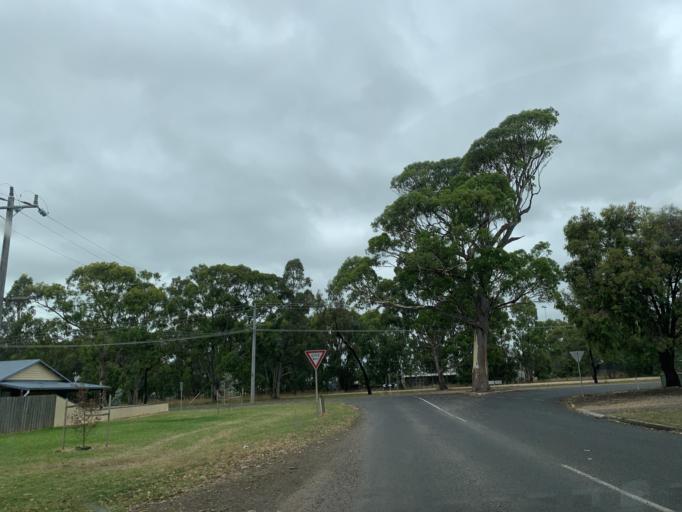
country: AU
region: Victoria
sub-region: Wellington
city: Heyfield
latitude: -37.9792
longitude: 146.7944
